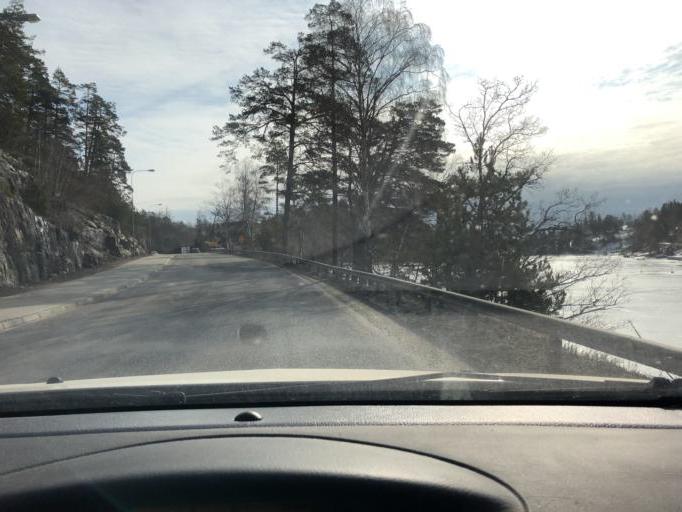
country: SE
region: Stockholm
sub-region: Nacka Kommun
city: Boo
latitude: 59.3341
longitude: 18.3026
